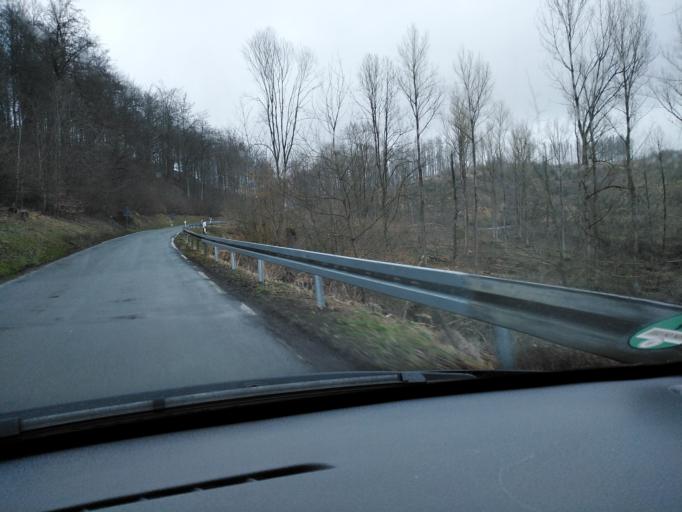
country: DE
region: North Rhine-Westphalia
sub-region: Regierungsbezirk Arnsberg
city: Brilon
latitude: 51.3815
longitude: 8.6341
